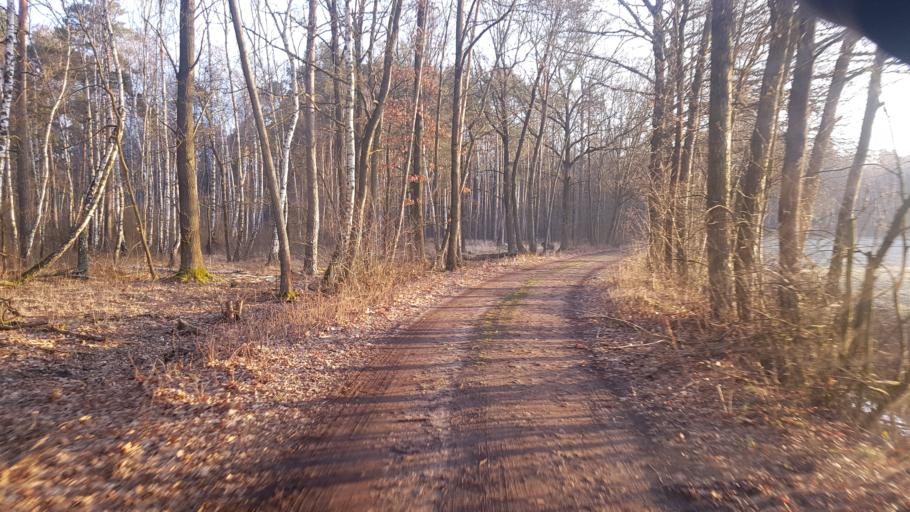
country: DE
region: Brandenburg
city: Finsterwalde
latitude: 51.6720
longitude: 13.7498
